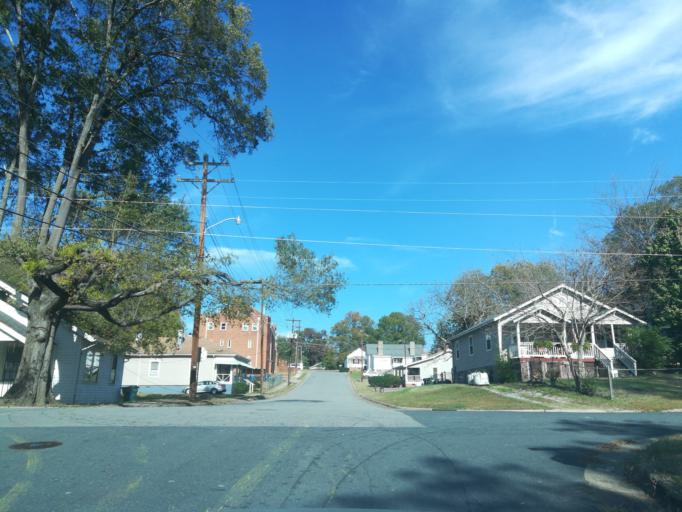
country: US
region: North Carolina
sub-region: Durham County
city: Durham
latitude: 35.9992
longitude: -78.8918
